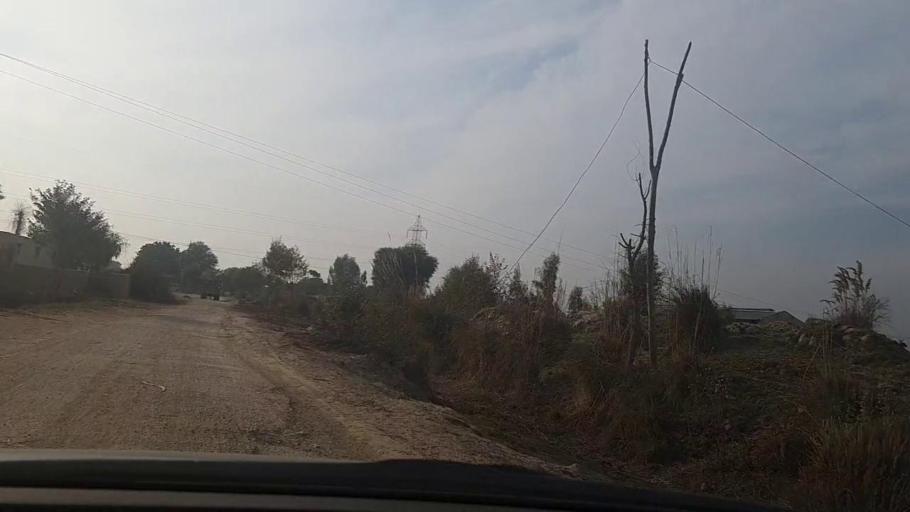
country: PK
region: Sindh
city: Daulatpur
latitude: 26.3311
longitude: 68.0805
